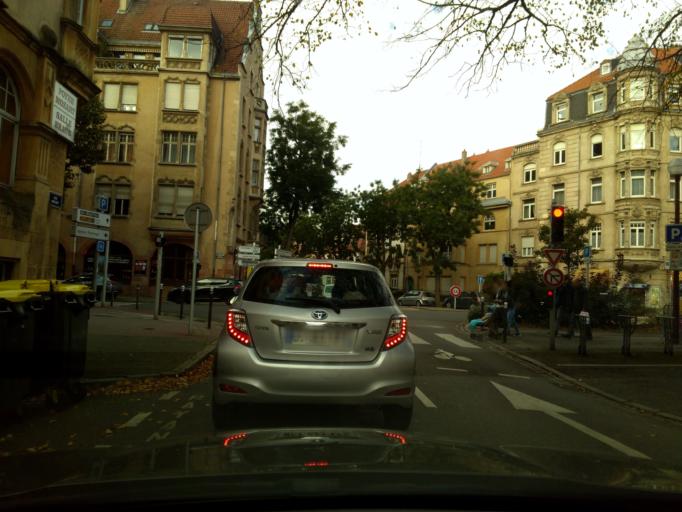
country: FR
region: Lorraine
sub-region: Departement de la Moselle
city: Metz
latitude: 49.1101
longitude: 6.1674
